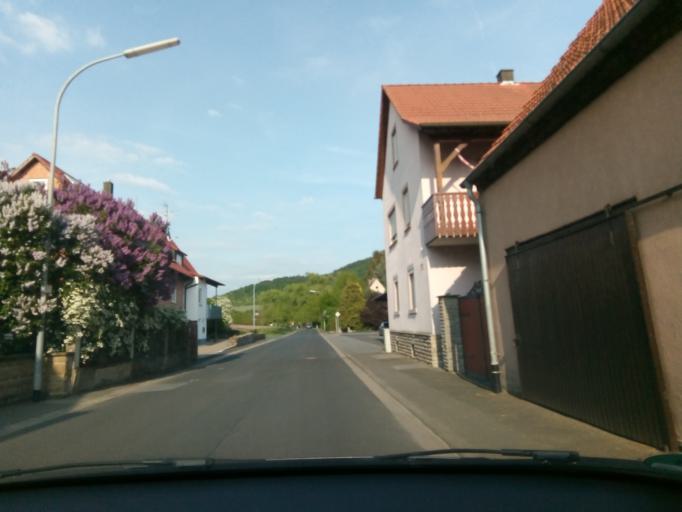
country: DE
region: Bavaria
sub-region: Regierungsbezirk Unterfranken
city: Oberschwarzach
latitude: 49.8610
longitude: 10.4125
